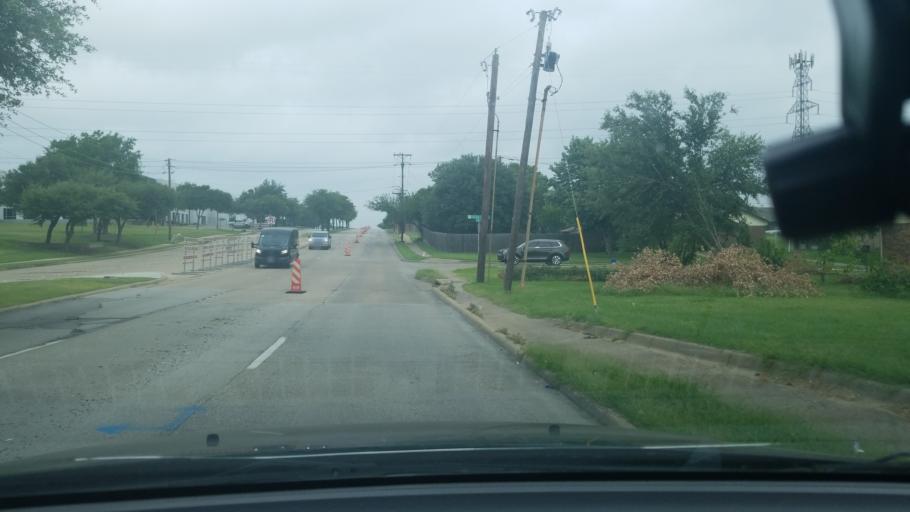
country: US
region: Texas
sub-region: Dallas County
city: Mesquite
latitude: 32.7833
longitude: -96.6479
